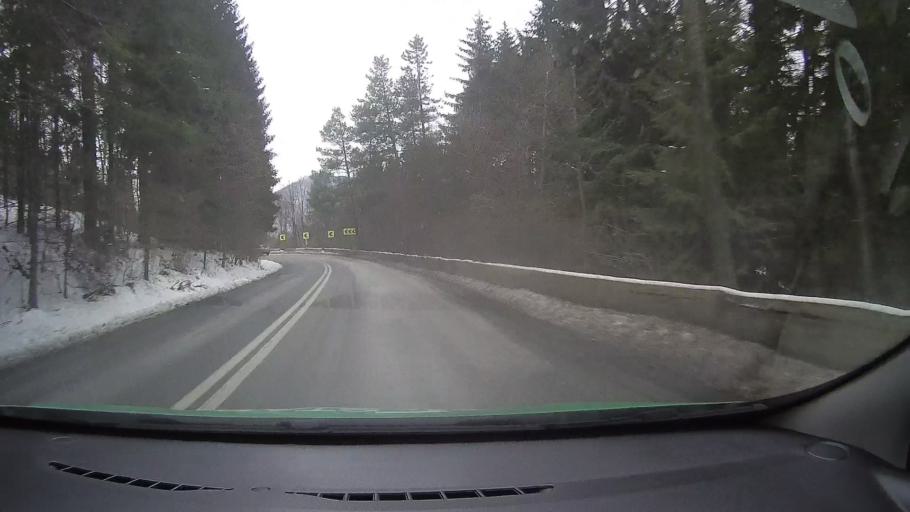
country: RO
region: Brasov
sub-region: Oras Predeal
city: Predeal
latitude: 45.5228
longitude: 25.5049
